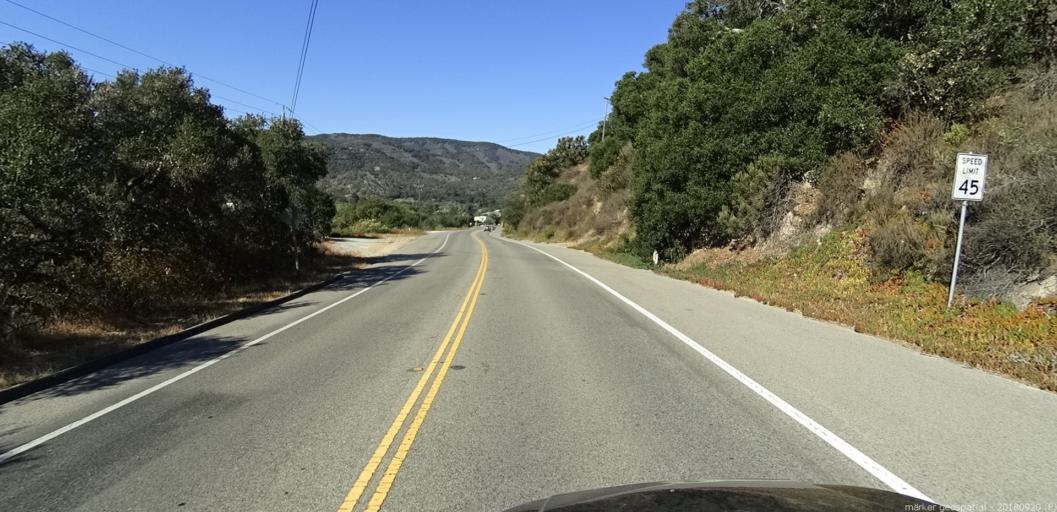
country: US
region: California
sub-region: Monterey County
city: Carmel Valley Village
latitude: 36.5239
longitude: -121.7999
